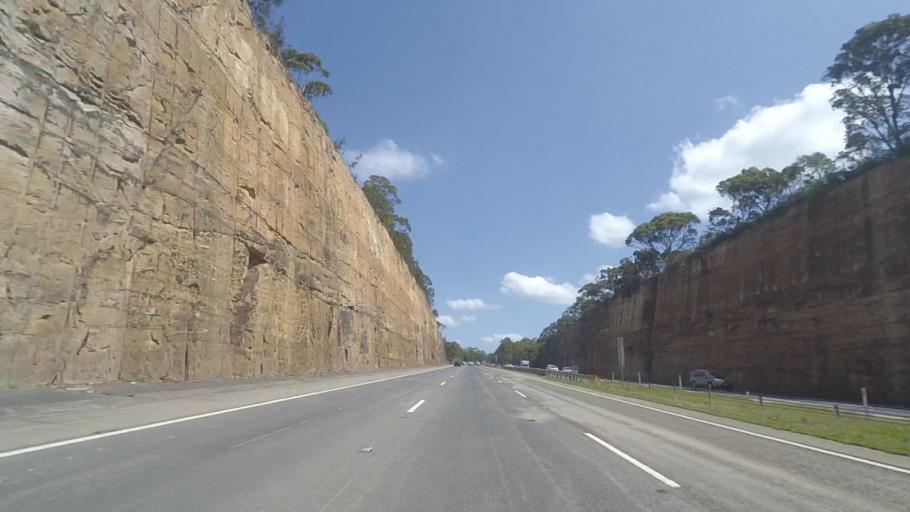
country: AU
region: New South Wales
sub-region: Hornsby Shire
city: Berowra
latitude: -33.6484
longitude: 151.1382
